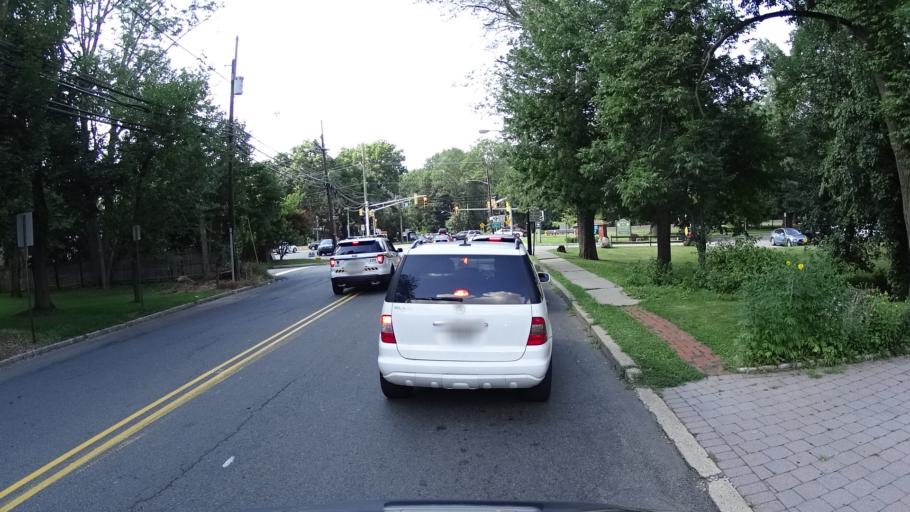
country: US
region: New Jersey
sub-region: Union County
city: Mountainside
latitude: 40.6710
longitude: -74.3572
